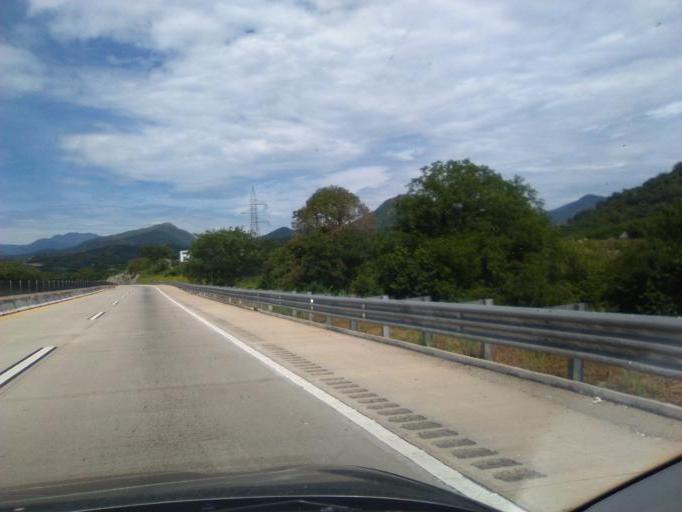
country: MX
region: Guerrero
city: Tierra Colorada
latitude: 17.1563
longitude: -99.5532
